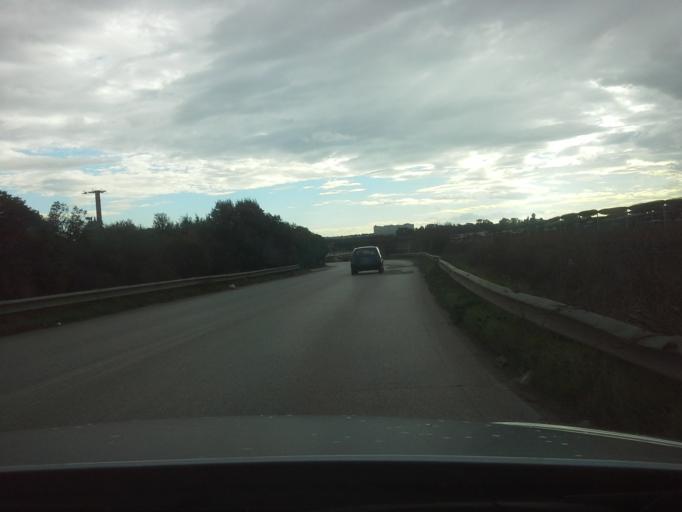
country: IT
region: Apulia
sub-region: Provincia di Bari
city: Cellamare
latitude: 41.0019
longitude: 16.9119
